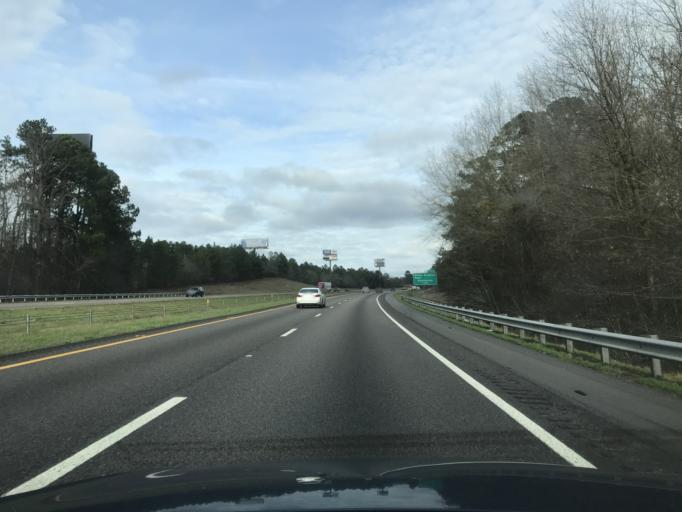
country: US
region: South Carolina
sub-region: Aiken County
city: Graniteville
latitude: 33.5984
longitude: -81.8687
